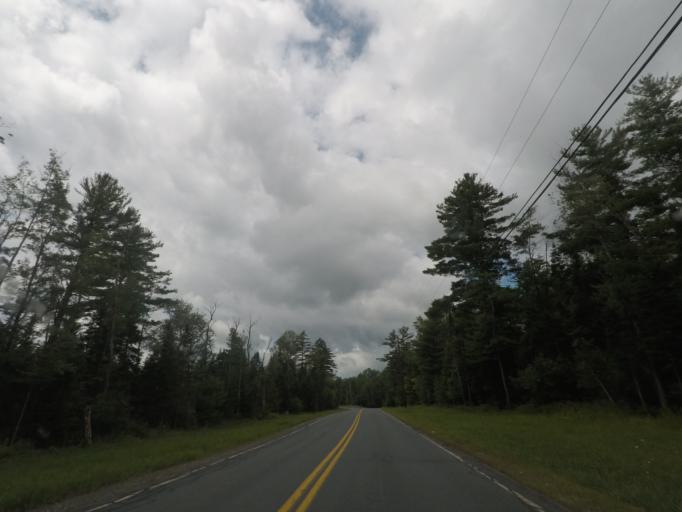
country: US
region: New York
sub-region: Rensselaer County
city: Poestenkill
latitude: 42.6918
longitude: -73.4293
